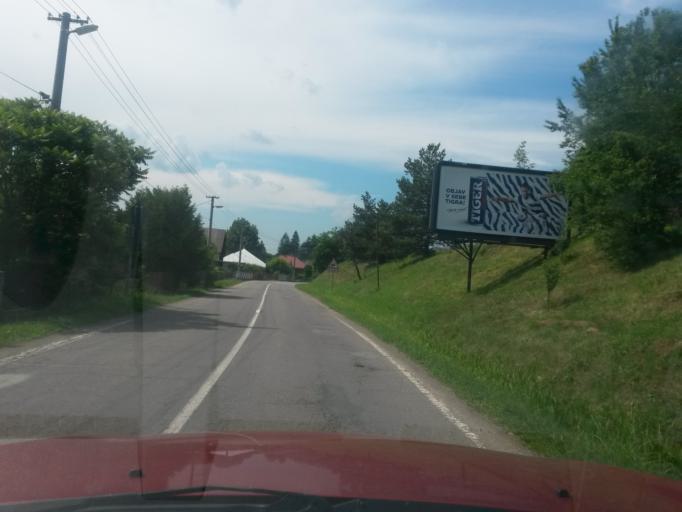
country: UA
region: Zakarpattia
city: Velykyi Bereznyi
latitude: 48.9009
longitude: 22.3875
